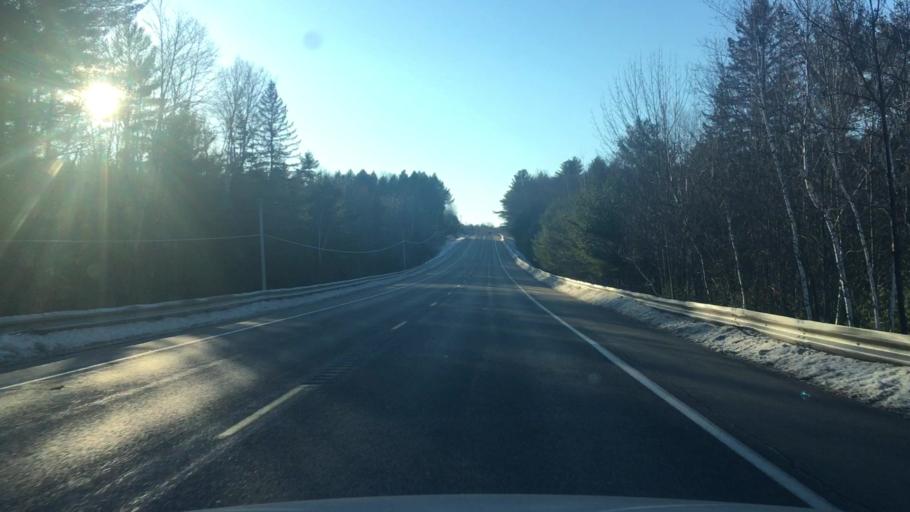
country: US
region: Maine
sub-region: Somerset County
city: Norridgewock
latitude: 44.6828
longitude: -69.8803
